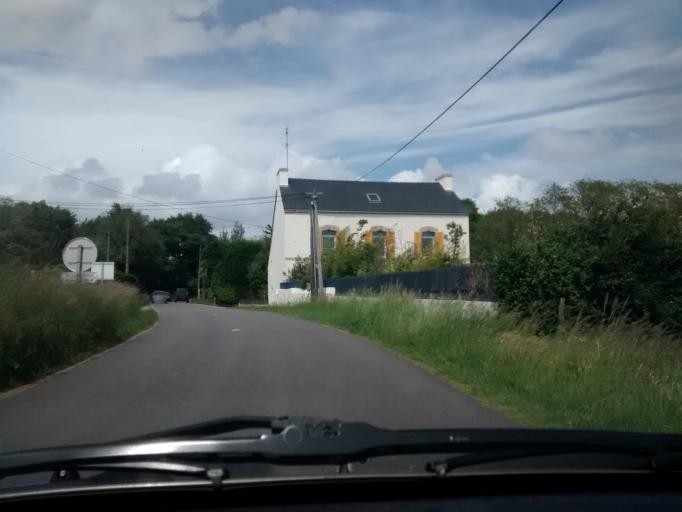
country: FR
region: Brittany
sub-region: Departement du Morbihan
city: Larmor-Baden
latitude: 47.5994
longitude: -2.8923
